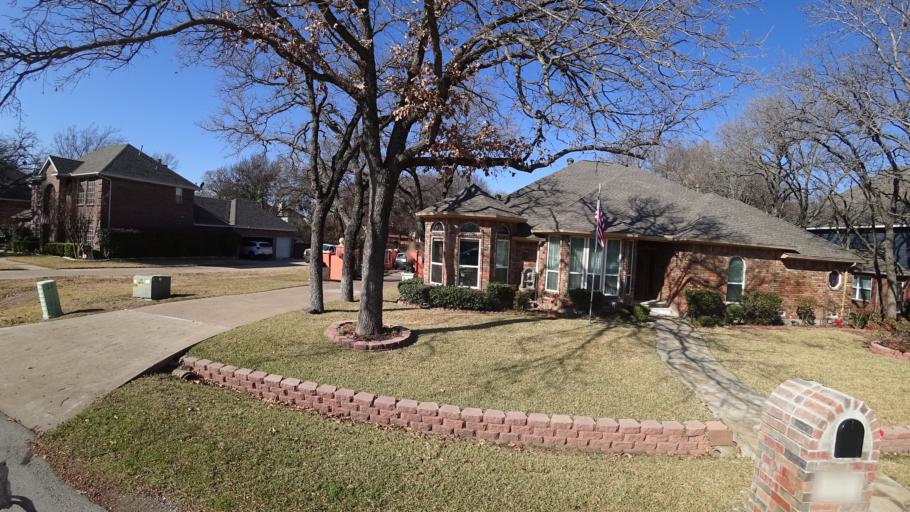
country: US
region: Texas
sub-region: Denton County
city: Lewisville
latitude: 33.0145
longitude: -97.0219
